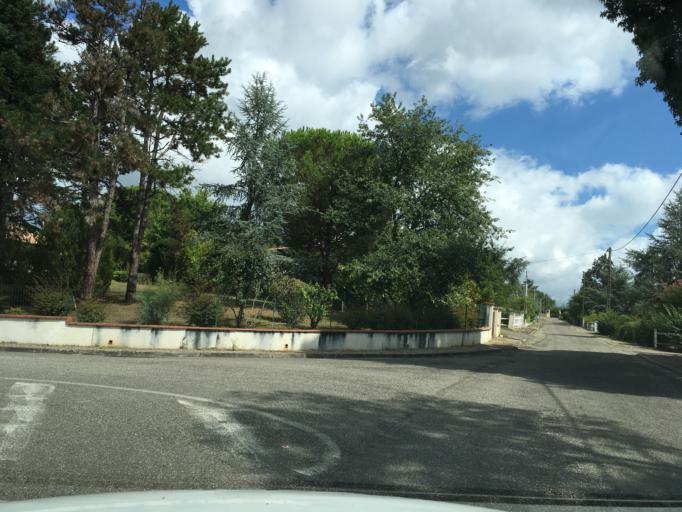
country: FR
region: Aquitaine
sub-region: Departement du Lot-et-Garonne
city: Foulayronnes
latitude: 44.2217
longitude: 0.6350
